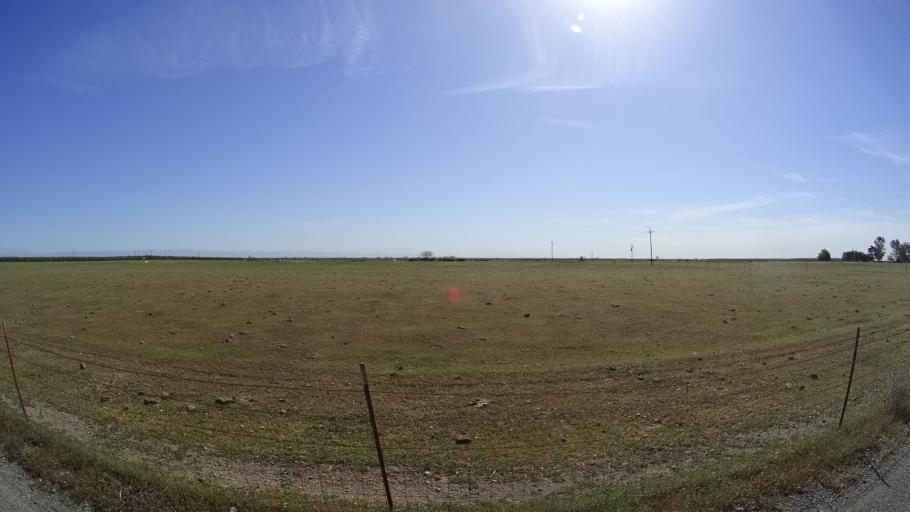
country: US
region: California
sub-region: Glenn County
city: Willows
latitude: 39.6218
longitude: -122.1565
